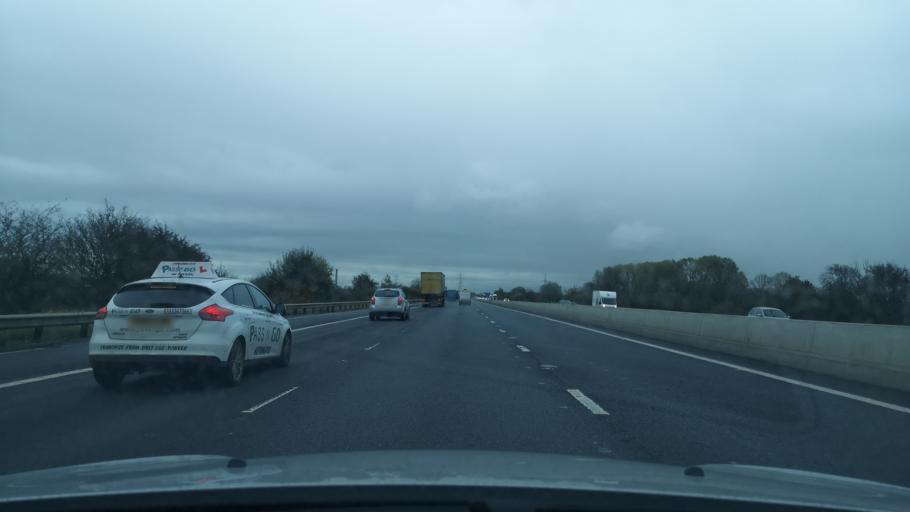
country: GB
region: England
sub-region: City and Borough of Wakefield
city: Knottingley
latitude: 53.6940
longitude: -1.2219
